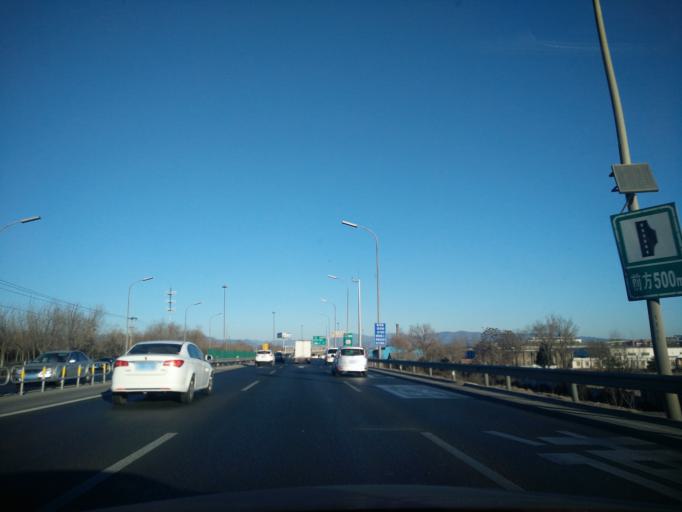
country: CN
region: Beijing
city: Fengtai
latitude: 39.8390
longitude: 116.2243
